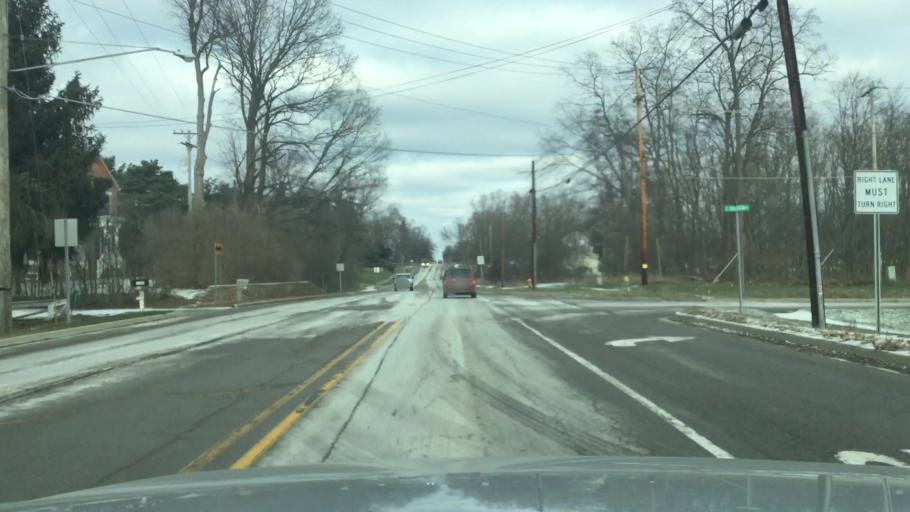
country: US
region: Michigan
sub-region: Genesee County
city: Linden
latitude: 42.8256
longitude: -83.7826
